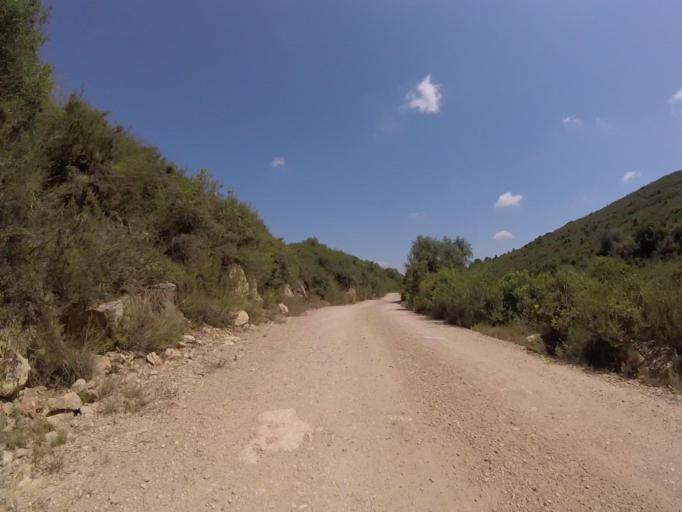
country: ES
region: Valencia
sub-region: Provincia de Castello
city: Torreblanca
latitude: 40.2262
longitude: 0.1555
